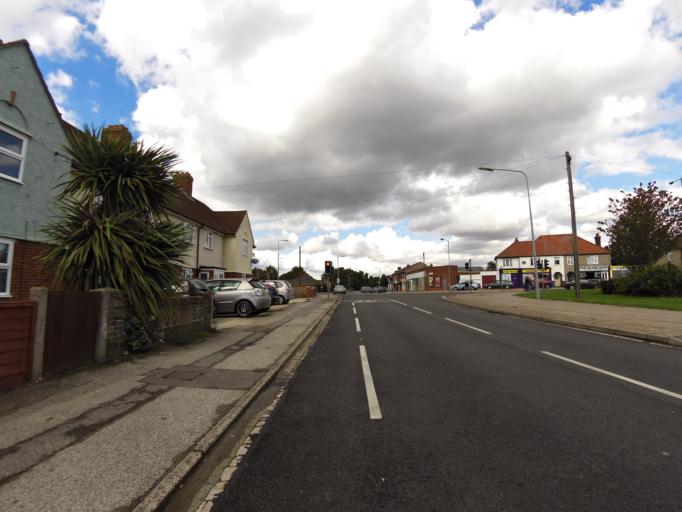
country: GB
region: England
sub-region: Suffolk
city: Ipswich
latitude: 52.0356
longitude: 1.1815
